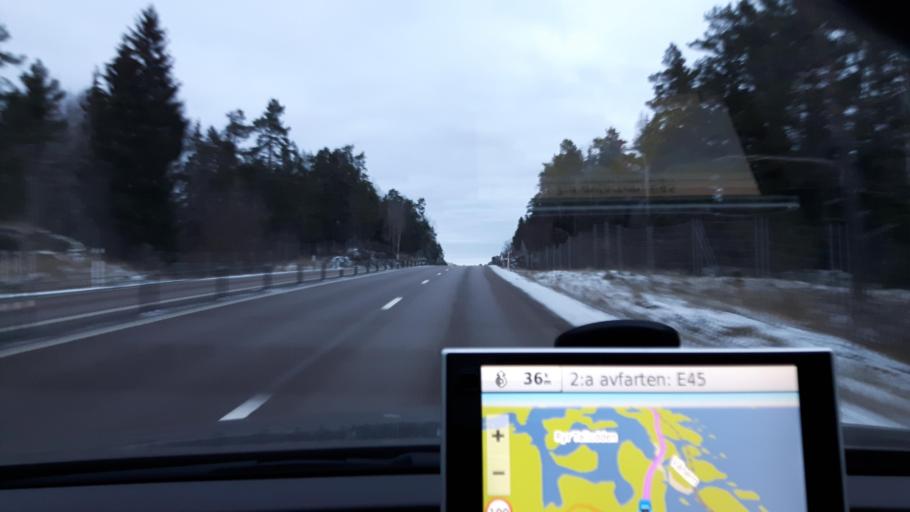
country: SE
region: Vaestra Goetaland
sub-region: Melleruds Kommun
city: Mellerud
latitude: 58.7687
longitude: 12.4918
